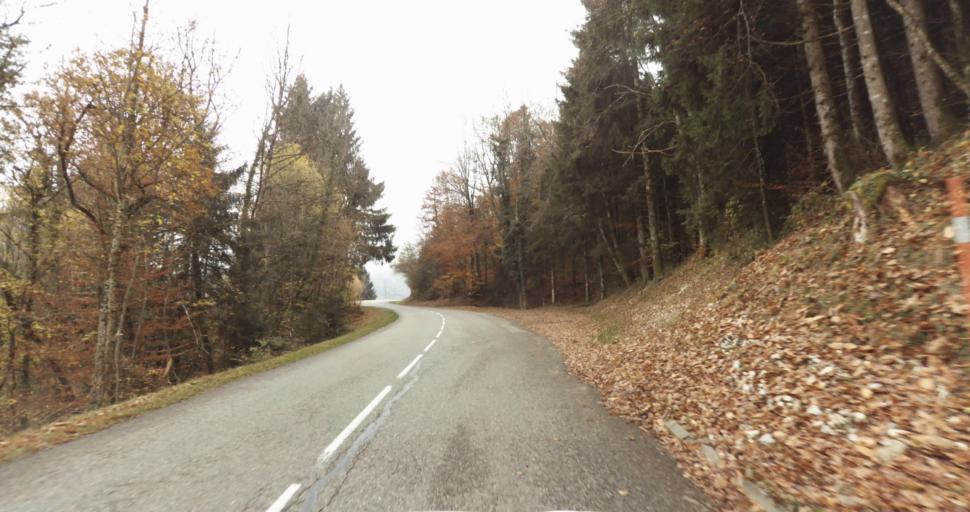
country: FR
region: Rhone-Alpes
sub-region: Departement de la Haute-Savoie
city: Saint-Jorioz
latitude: 45.8037
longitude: 6.1370
